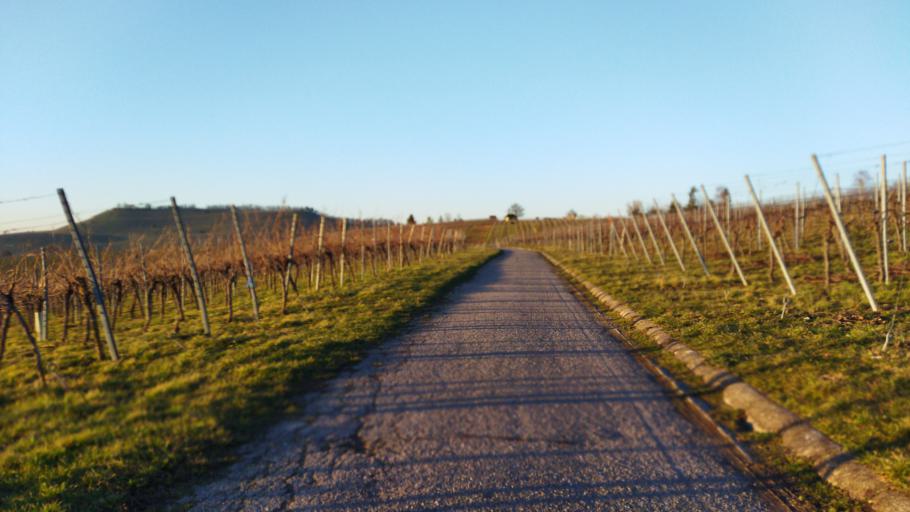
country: DE
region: Baden-Wuerttemberg
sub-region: Regierungsbezirk Stuttgart
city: Erlenbach
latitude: 49.1832
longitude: 9.2650
